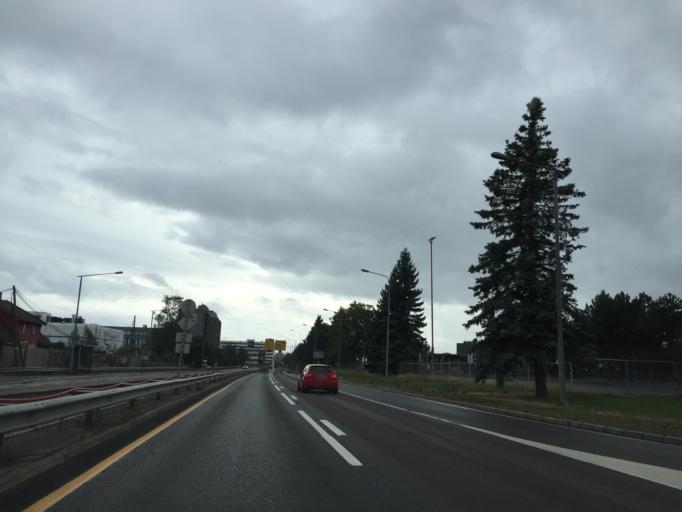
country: NO
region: Oslo
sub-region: Oslo
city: Oslo
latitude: 59.9311
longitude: 10.8236
